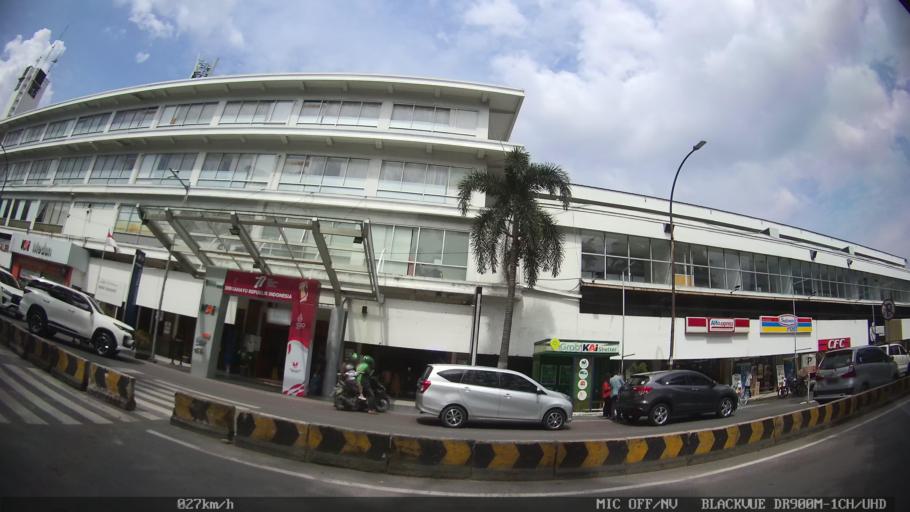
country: ID
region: North Sumatra
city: Medan
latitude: 3.5906
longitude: 98.6794
